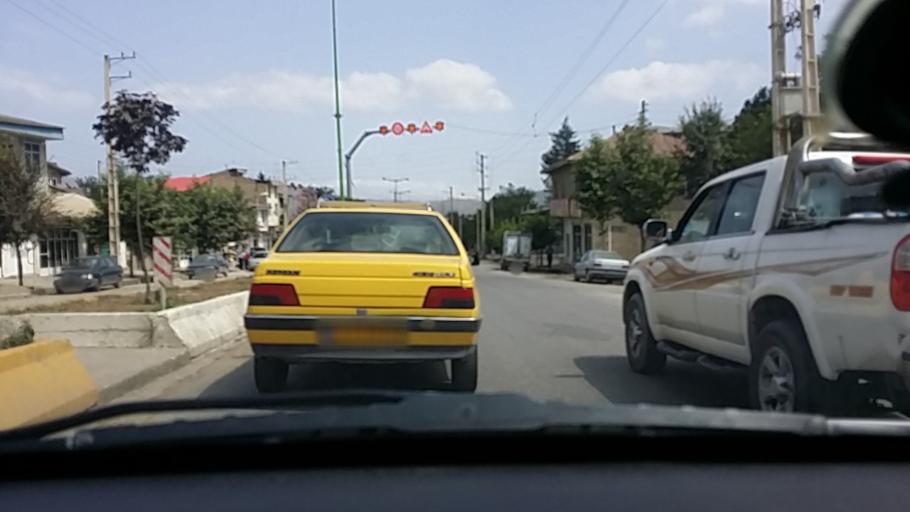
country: IR
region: Mazandaran
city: `Abbasabad
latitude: 36.5080
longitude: 51.1842
